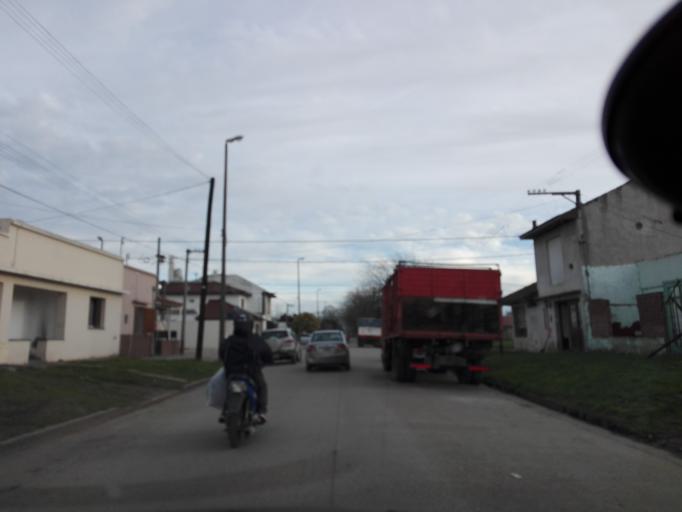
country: AR
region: Buenos Aires
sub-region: Partido de Balcarce
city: Balcarce
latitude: -37.8432
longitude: -58.2475
